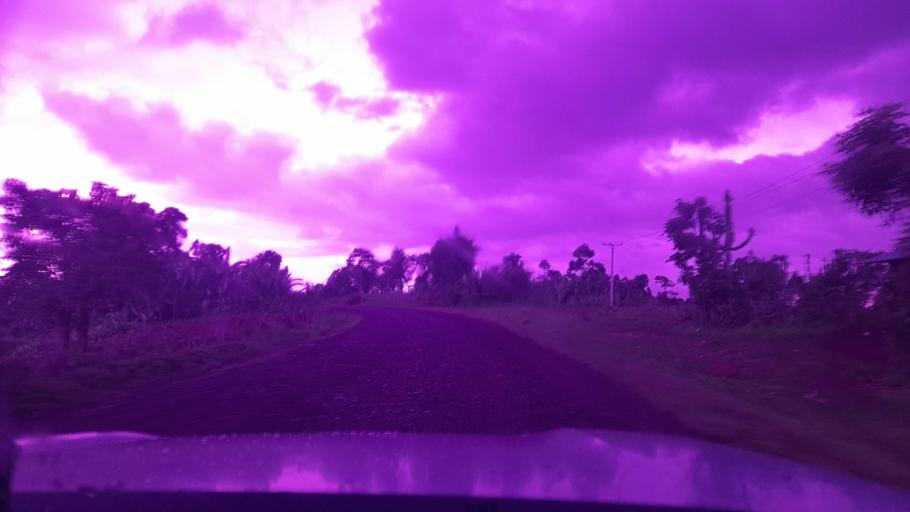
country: ET
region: Southern Nations, Nationalities, and People's Region
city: Mizan Teferi
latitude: 6.9155
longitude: 35.8425
